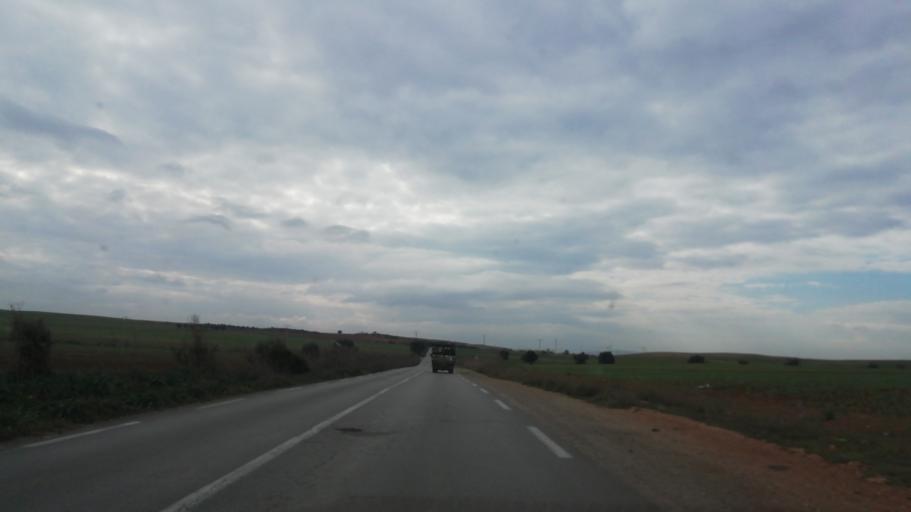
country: DZ
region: Oran
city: Ain el Bya
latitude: 35.7588
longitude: -0.3503
